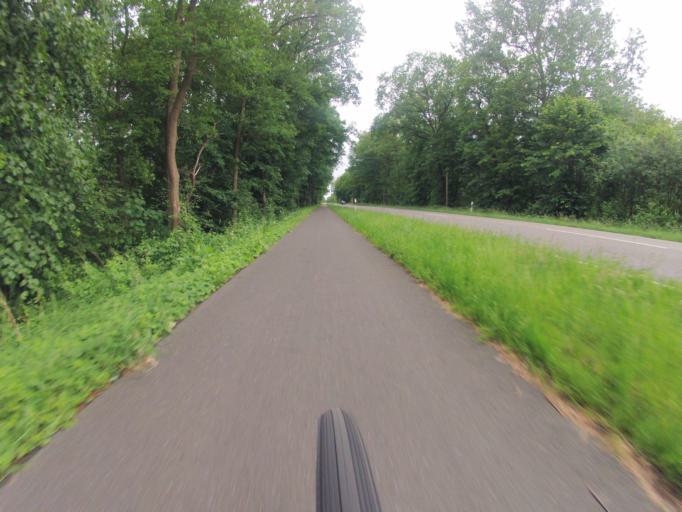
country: DE
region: North Rhine-Westphalia
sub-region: Regierungsbezirk Munster
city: Saerbeck
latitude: 52.2029
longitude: 7.6691
